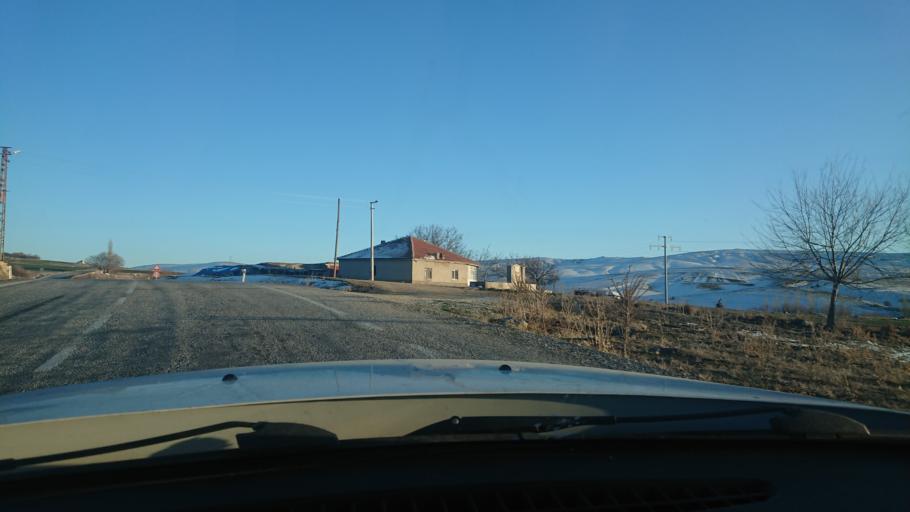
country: TR
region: Aksaray
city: Ortakoy
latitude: 38.7543
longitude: 33.9326
